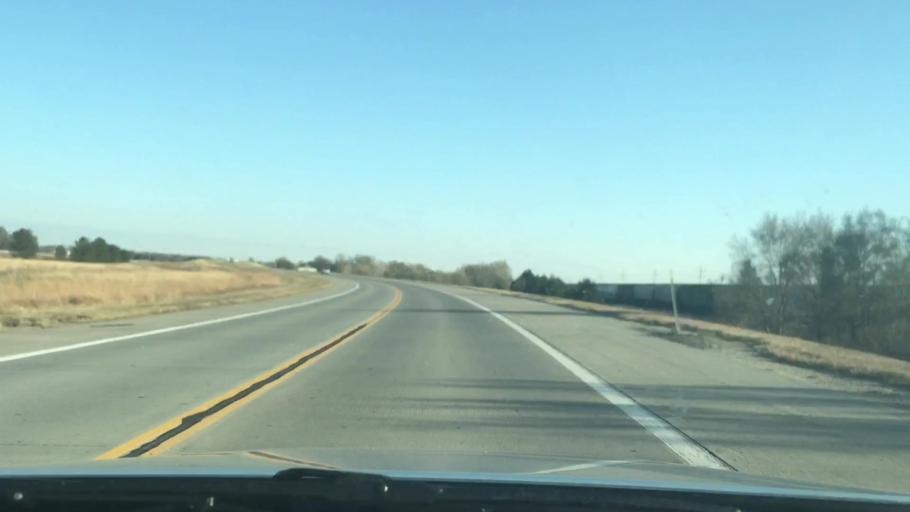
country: US
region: Kansas
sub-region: Reno County
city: Nickerson
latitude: 38.1059
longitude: -98.0229
